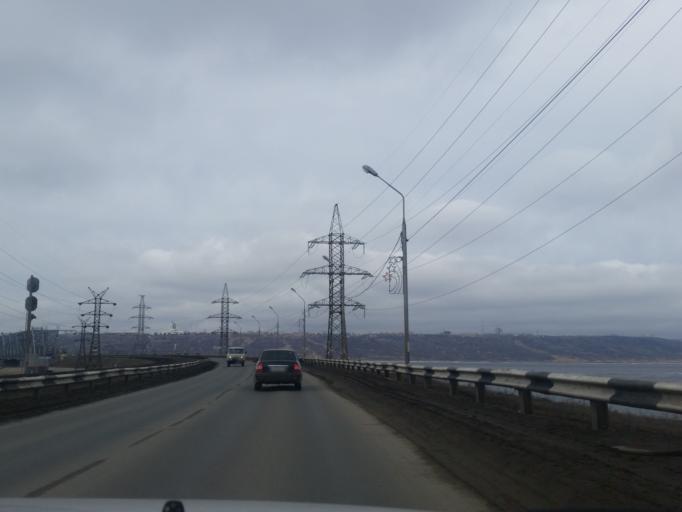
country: RU
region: Ulyanovsk
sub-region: Ulyanovskiy Rayon
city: Ulyanovsk
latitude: 54.3198
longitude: 48.4656
